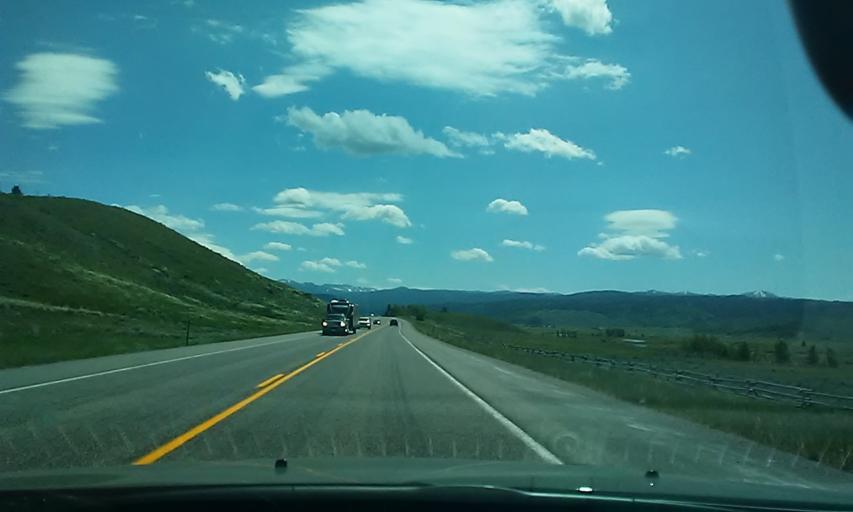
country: US
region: Wyoming
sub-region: Teton County
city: Jackson
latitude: 43.8396
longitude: -110.4520
